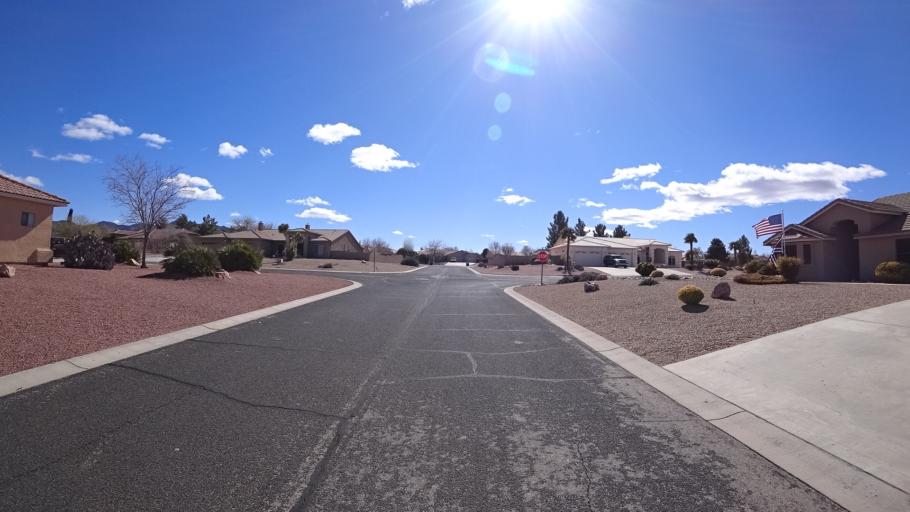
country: US
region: Arizona
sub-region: Mohave County
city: Kingman
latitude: 35.2055
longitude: -113.9732
